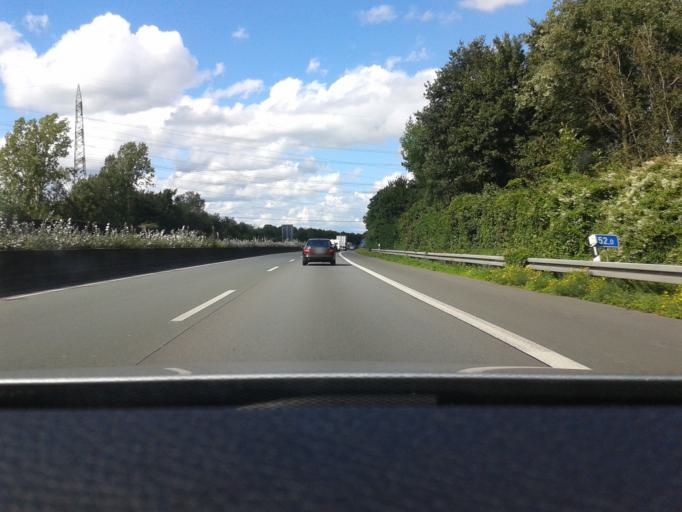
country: DE
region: North Rhine-Westphalia
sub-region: Regierungsbezirk Dusseldorf
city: Moers
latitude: 51.4489
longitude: 6.5956
